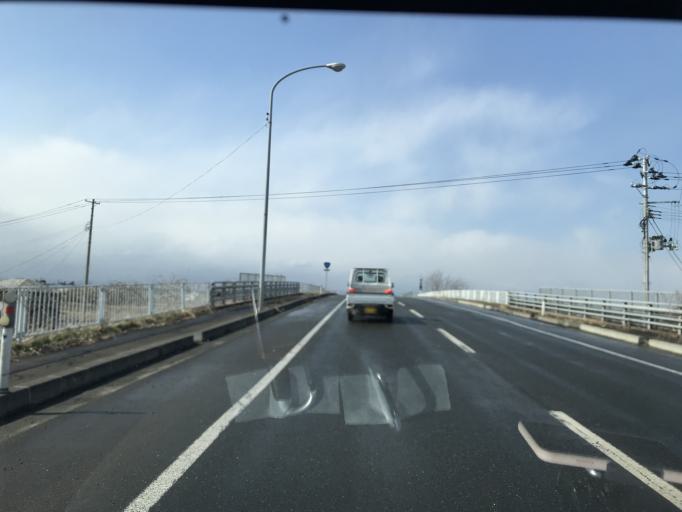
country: JP
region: Iwate
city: Kitakami
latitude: 39.2967
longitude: 141.0834
